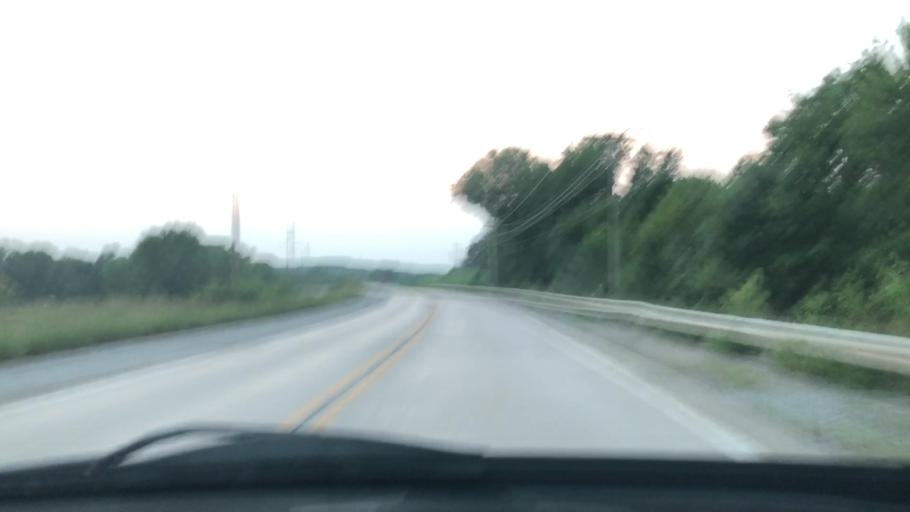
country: US
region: Iowa
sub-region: Johnson County
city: North Liberty
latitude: 41.8102
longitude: -91.6564
